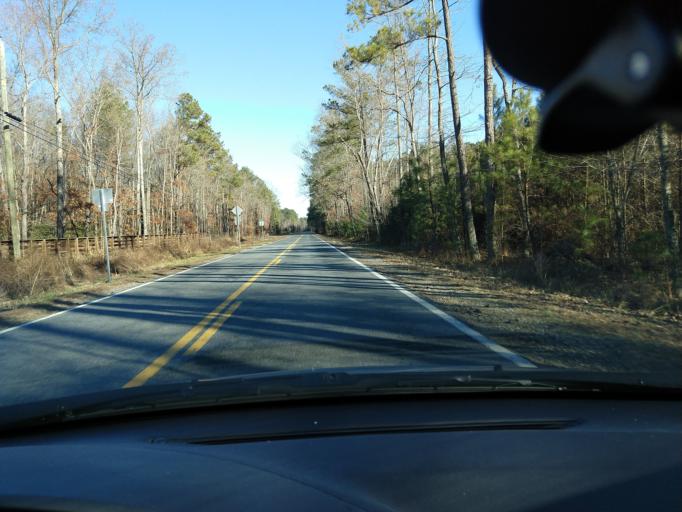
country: US
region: Virginia
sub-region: Charles City County
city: Charles City
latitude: 37.3257
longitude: -76.9974
